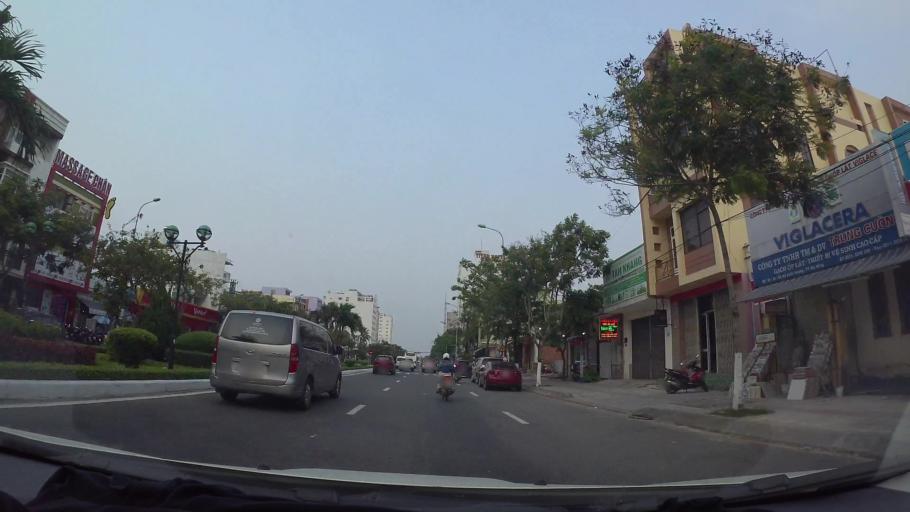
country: VN
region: Da Nang
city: Ngu Hanh Son
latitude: 16.0393
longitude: 108.2455
